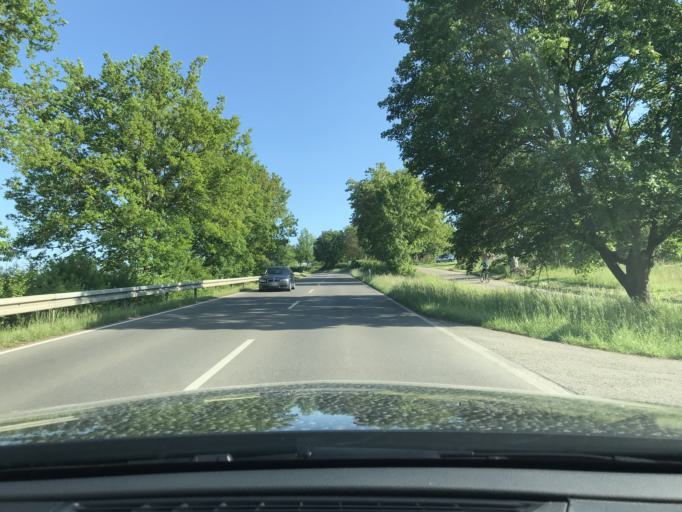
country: DE
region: Baden-Wuerttemberg
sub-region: Regierungsbezirk Stuttgart
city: Schwaikheim
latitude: 48.8791
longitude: 9.3182
